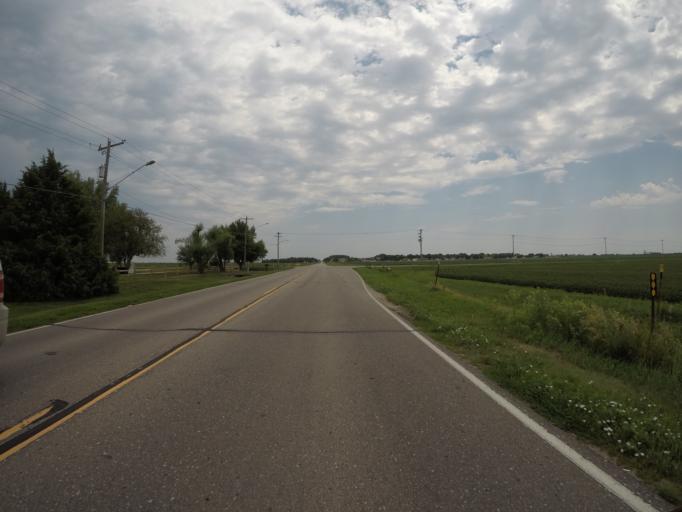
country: US
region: Nebraska
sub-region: Adams County
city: Hastings
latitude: 40.5970
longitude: -98.4407
